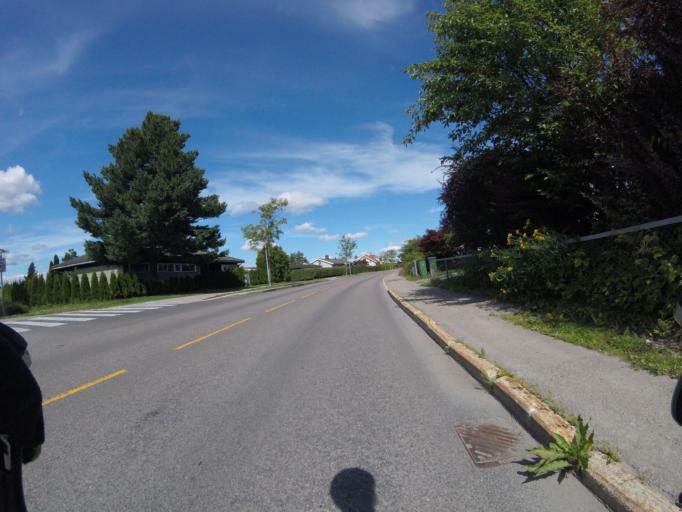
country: NO
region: Akershus
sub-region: Skedsmo
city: Lillestrom
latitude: 59.9428
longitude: 11.0158
